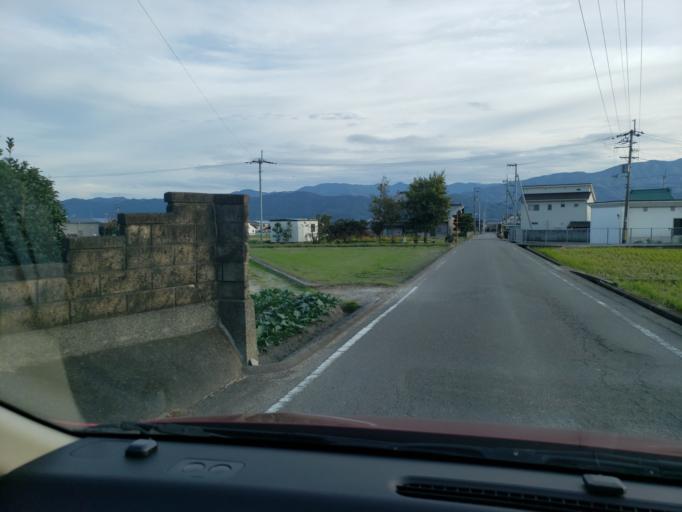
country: JP
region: Tokushima
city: Wakimachi
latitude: 34.0910
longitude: 134.2259
